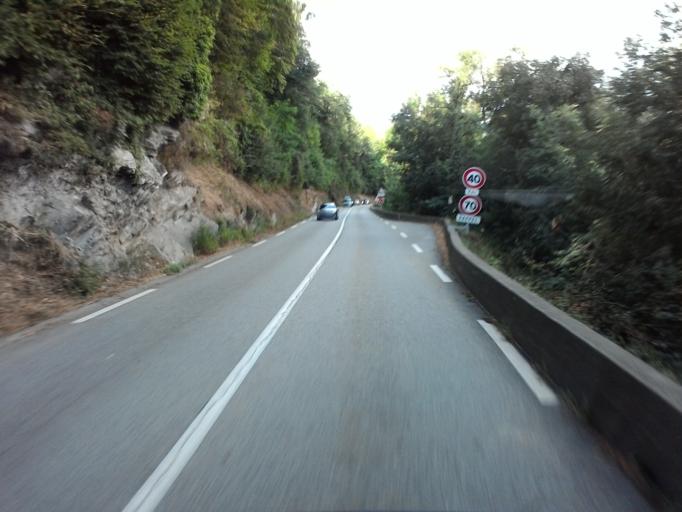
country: FR
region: Rhone-Alpes
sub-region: Departement de l'Isere
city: Notre-Dame-de-Mesage
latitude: 45.0683
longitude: 5.7552
